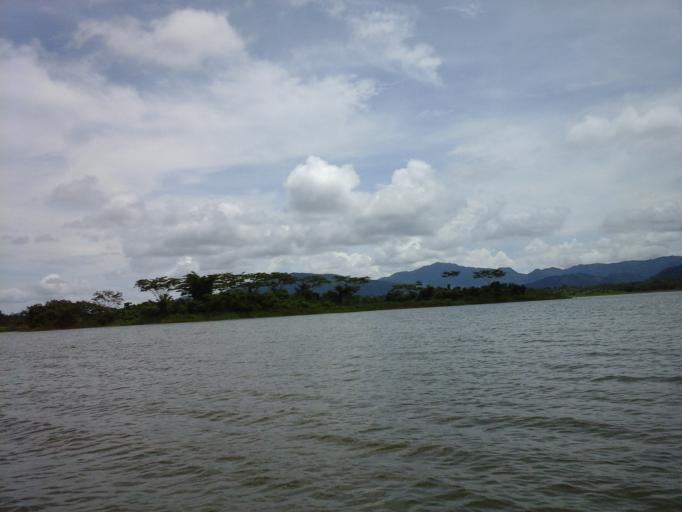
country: CO
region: Bolivar
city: San Cristobal
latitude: 9.8765
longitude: -75.3030
